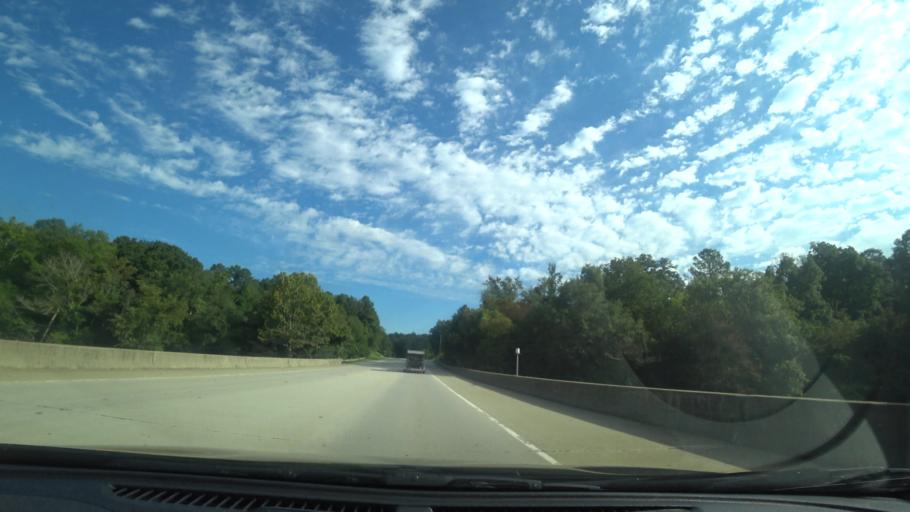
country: US
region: Georgia
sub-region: Rockdale County
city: Conyers
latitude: 33.6922
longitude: -83.9968
